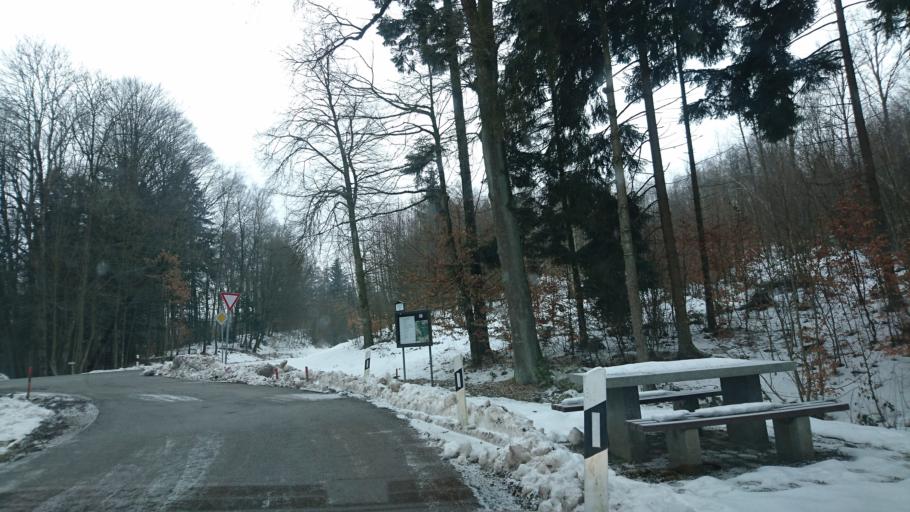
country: DE
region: Bavaria
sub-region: Lower Bavaria
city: Bad Griesbach
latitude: 48.4707
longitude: 13.2018
